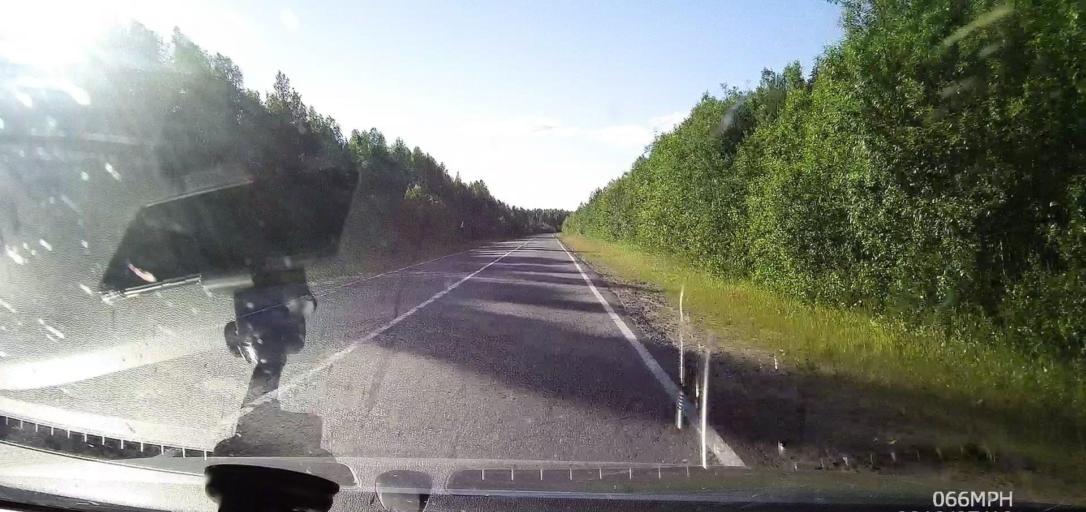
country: RU
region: Arkhangelskaya
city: Samoded
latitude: 63.3382
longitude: 40.4856
